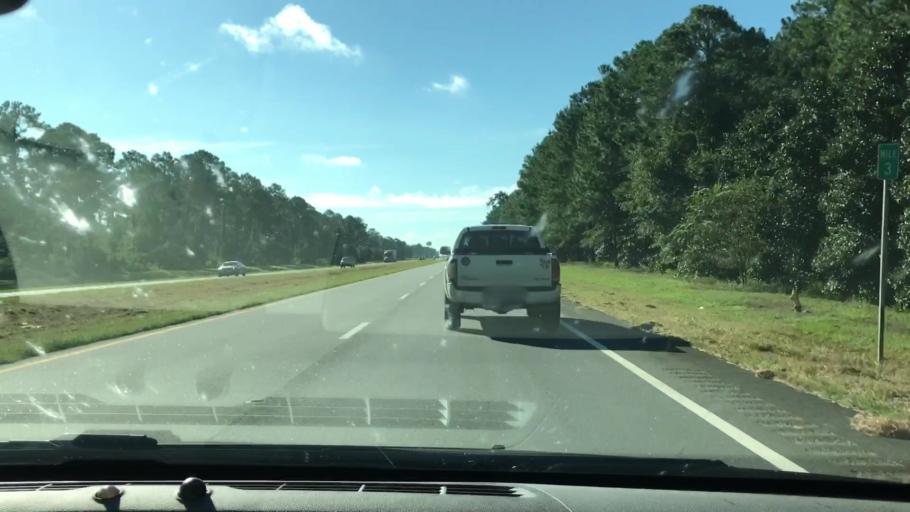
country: US
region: Georgia
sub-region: Lee County
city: Leesburg
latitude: 31.6527
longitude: -84.2668
